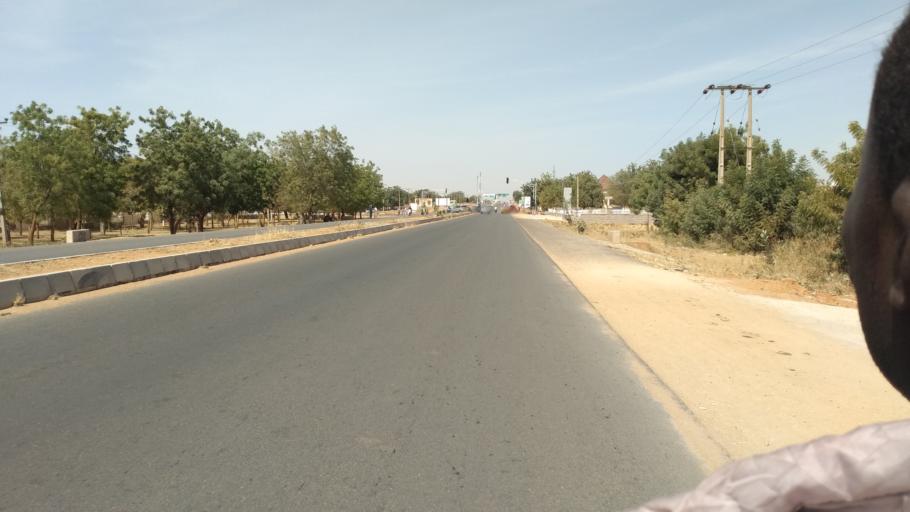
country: NG
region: Jigawa
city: Dutse
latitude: 11.6836
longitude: 9.3398
